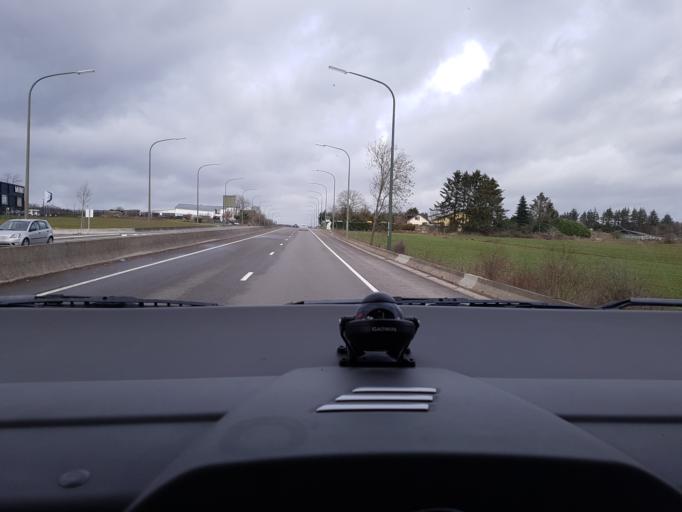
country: BE
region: Wallonia
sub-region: Province du Luxembourg
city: Marche-en-Famenne
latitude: 50.2418
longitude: 5.2909
